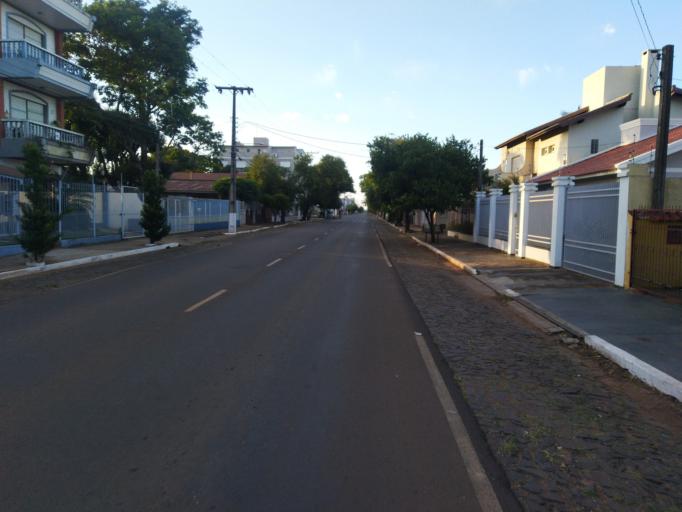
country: BR
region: Rio Grande do Sul
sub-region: Sao Borja
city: Sao Borja
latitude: -28.6588
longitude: -56.0093
